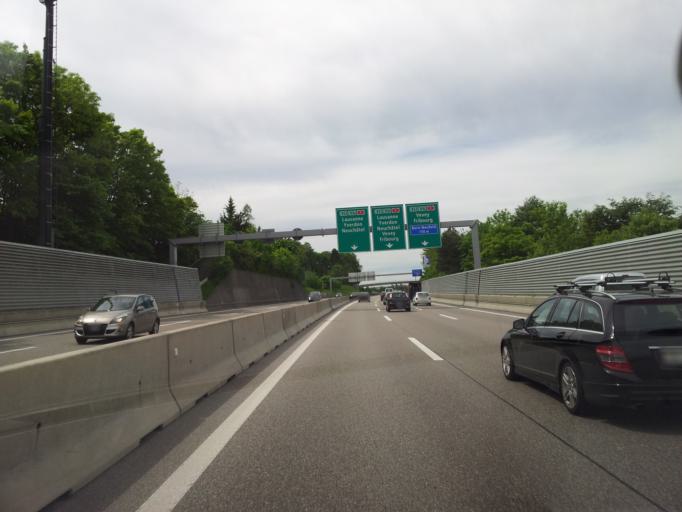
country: CH
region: Bern
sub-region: Bern-Mittelland District
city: Bern
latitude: 46.9674
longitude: 7.4411
